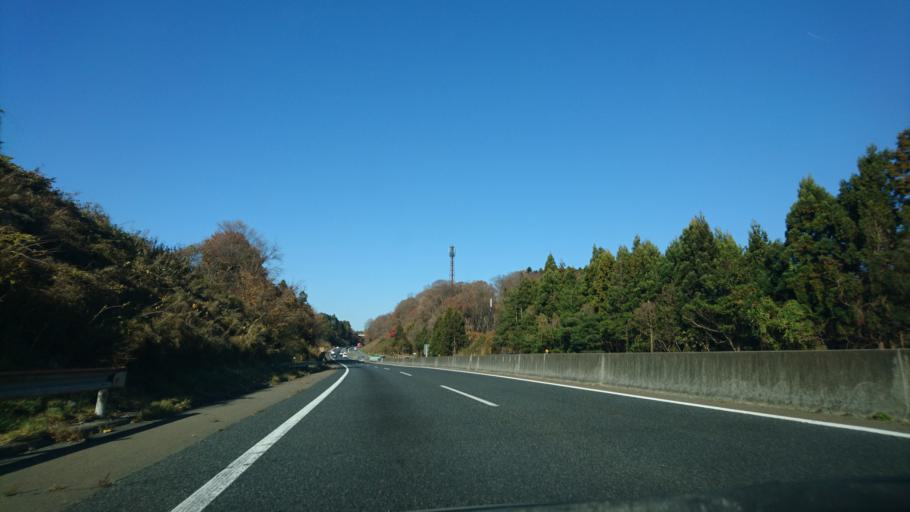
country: JP
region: Miyagi
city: Tomiya
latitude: 38.3548
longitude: 140.8815
